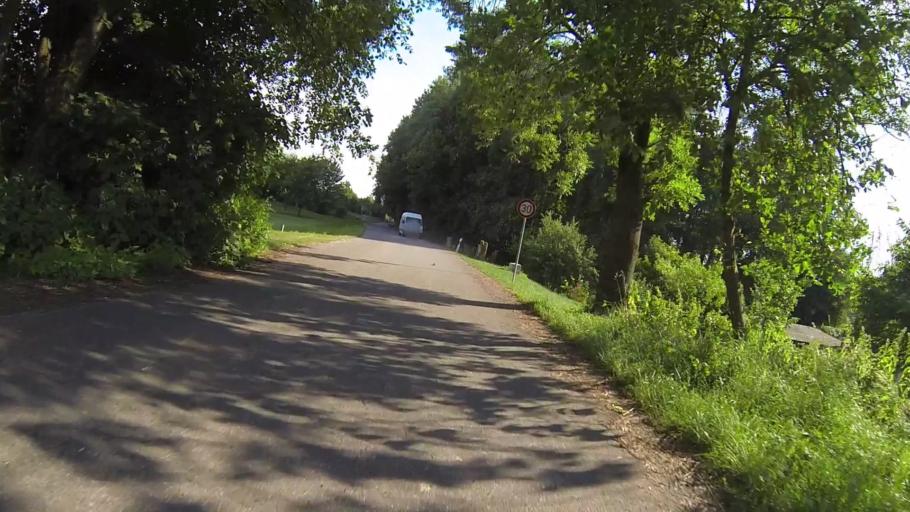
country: DE
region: Bavaria
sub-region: Swabia
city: Neu-Ulm
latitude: 48.4142
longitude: 10.0184
